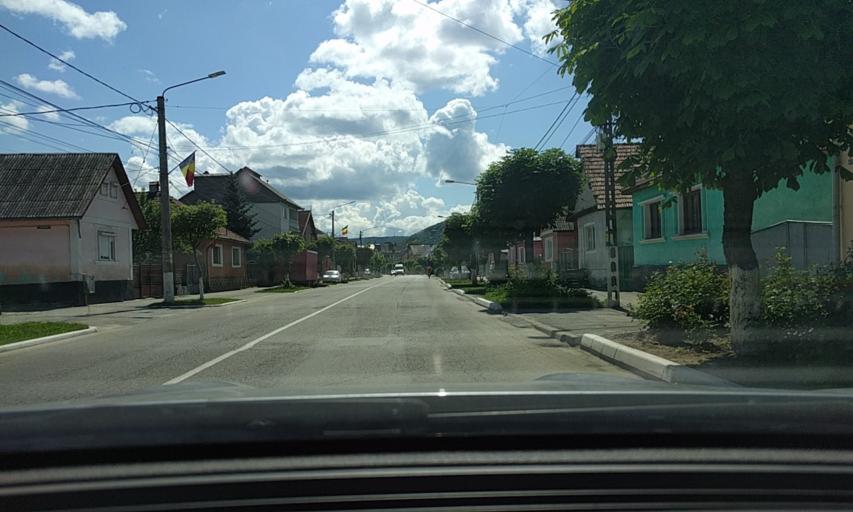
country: RO
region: Bistrita-Nasaud
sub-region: Oras Nasaud
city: Nasaud
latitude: 47.2882
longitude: 24.3942
